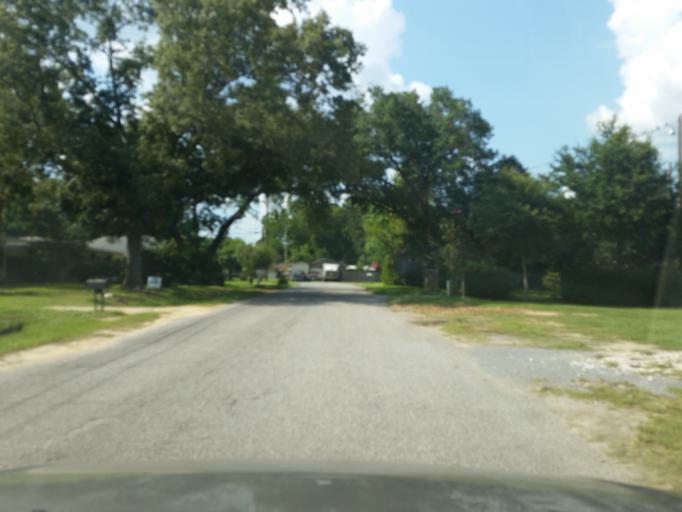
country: US
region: Florida
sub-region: Escambia County
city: Ferry Pass
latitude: 30.4984
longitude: -87.2142
